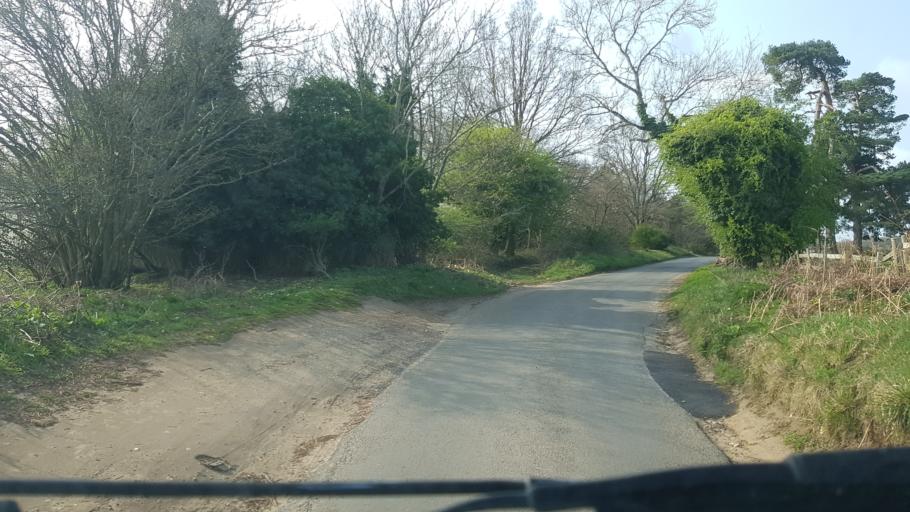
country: GB
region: England
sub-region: Surrey
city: Chilworth
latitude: 51.2253
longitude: -0.5161
